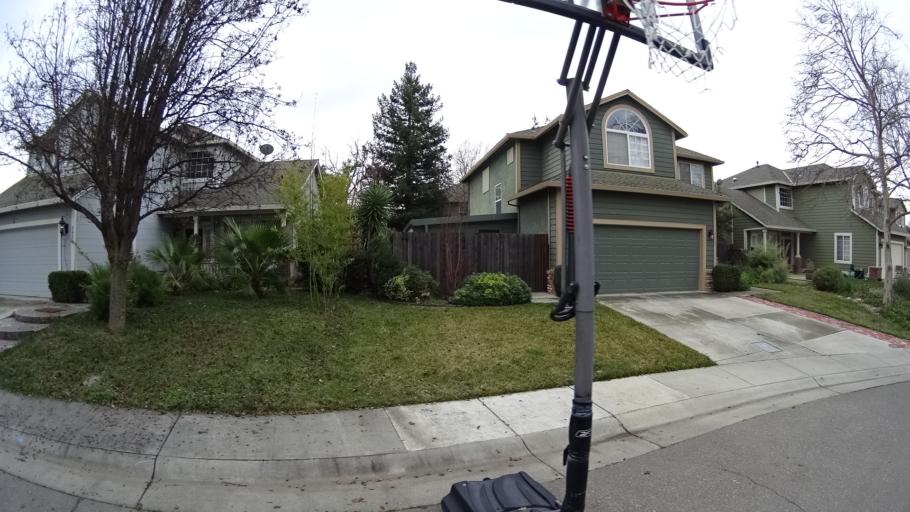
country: US
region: California
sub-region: Yolo County
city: Davis
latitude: 38.5564
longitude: -121.7187
